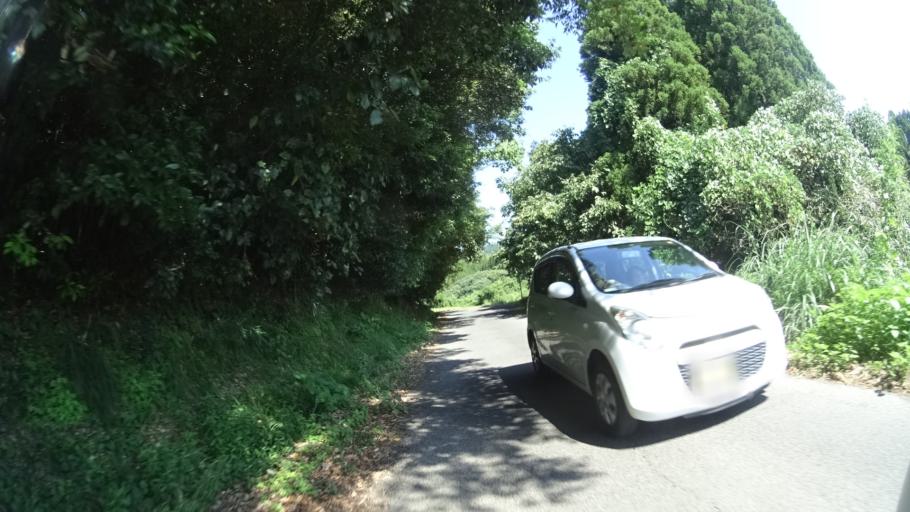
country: JP
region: Kagoshima
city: Kajiki
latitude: 31.7533
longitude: 130.6714
